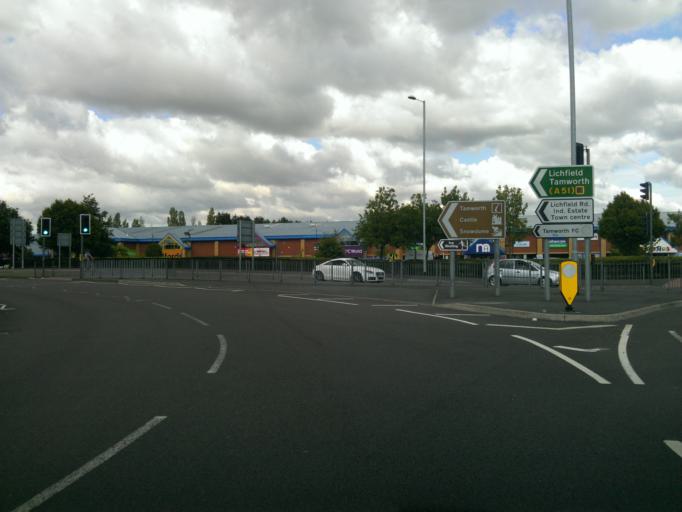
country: GB
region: England
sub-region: Staffordshire
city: Tamworth
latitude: 52.6271
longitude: -1.7044
